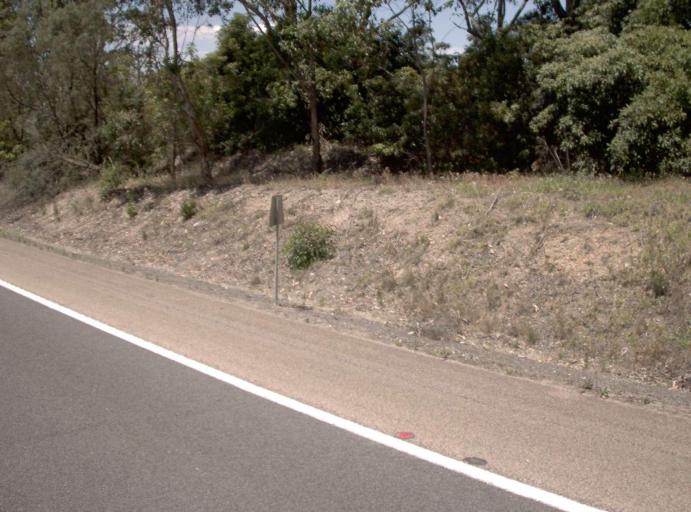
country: AU
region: Victoria
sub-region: East Gippsland
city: Lakes Entrance
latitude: -37.7027
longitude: 148.5569
